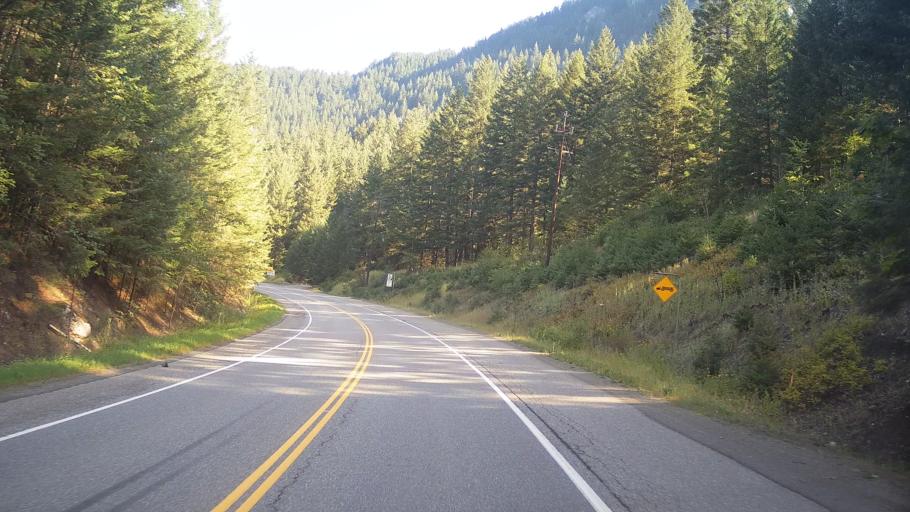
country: CA
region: British Columbia
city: Hope
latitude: 49.7040
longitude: -121.4088
